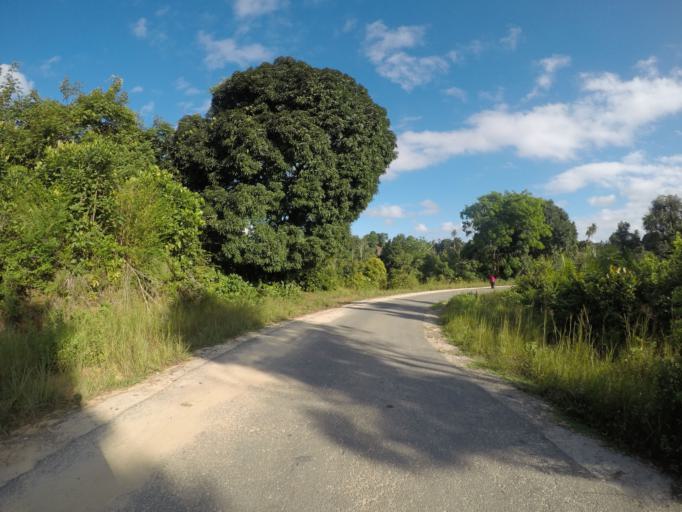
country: TZ
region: Pemba South
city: Mtambile
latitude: -5.3547
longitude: 39.7082
